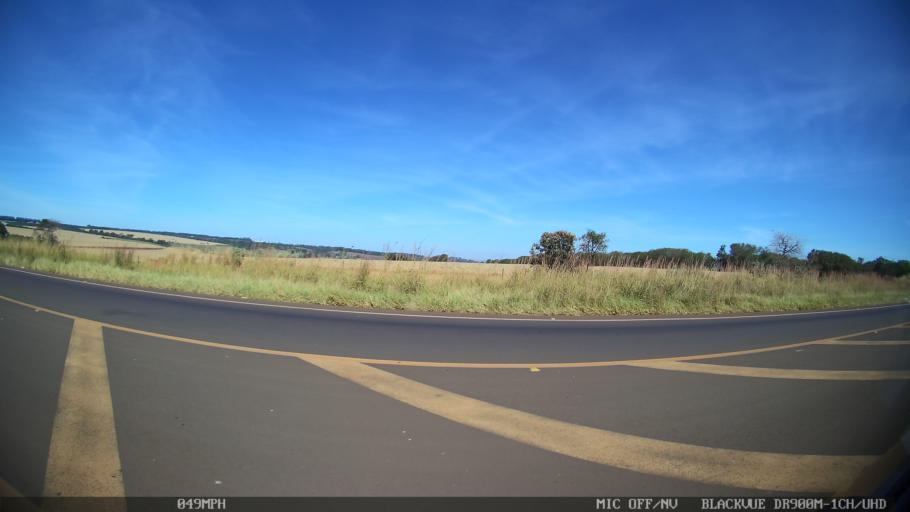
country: BR
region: Sao Paulo
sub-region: Franca
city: Franca
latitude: -20.5462
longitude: -47.4711
